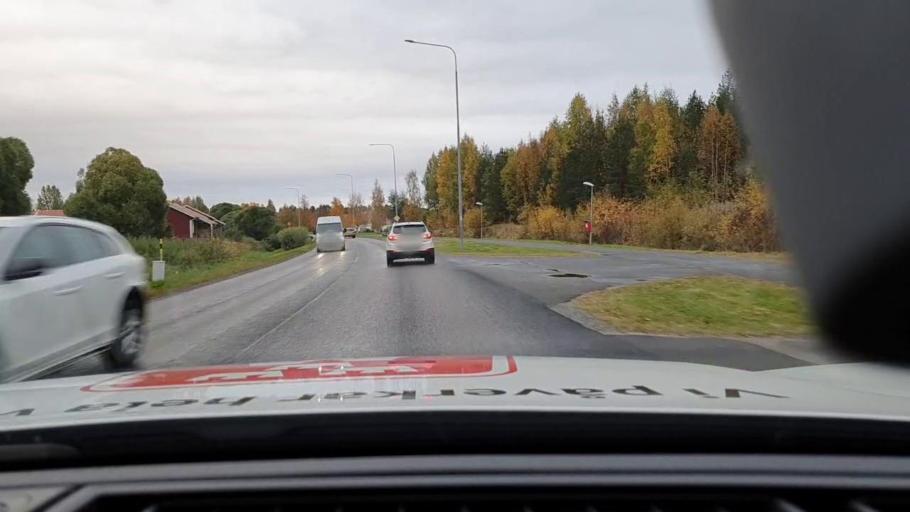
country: SE
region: Norrbotten
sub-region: Bodens Kommun
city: Saevast
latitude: 65.7594
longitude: 21.7406
